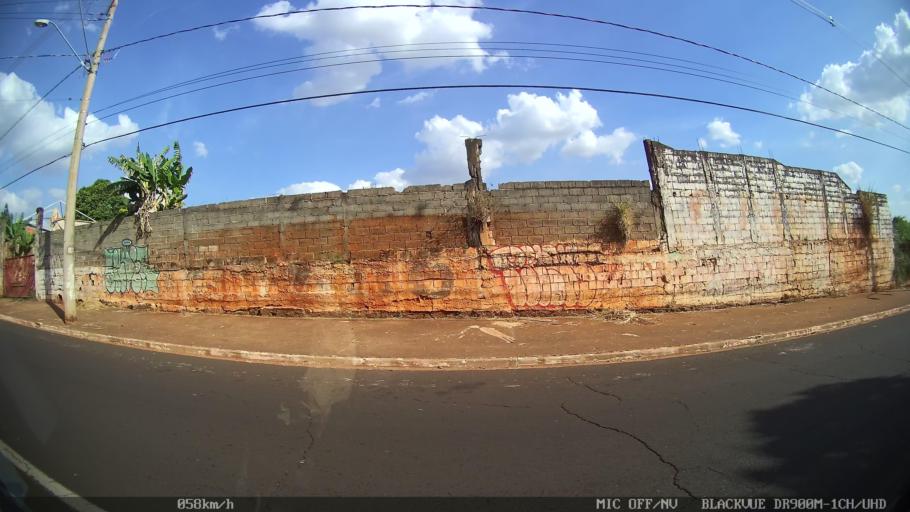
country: BR
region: Sao Paulo
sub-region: Ribeirao Preto
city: Ribeirao Preto
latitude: -21.1863
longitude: -47.8376
